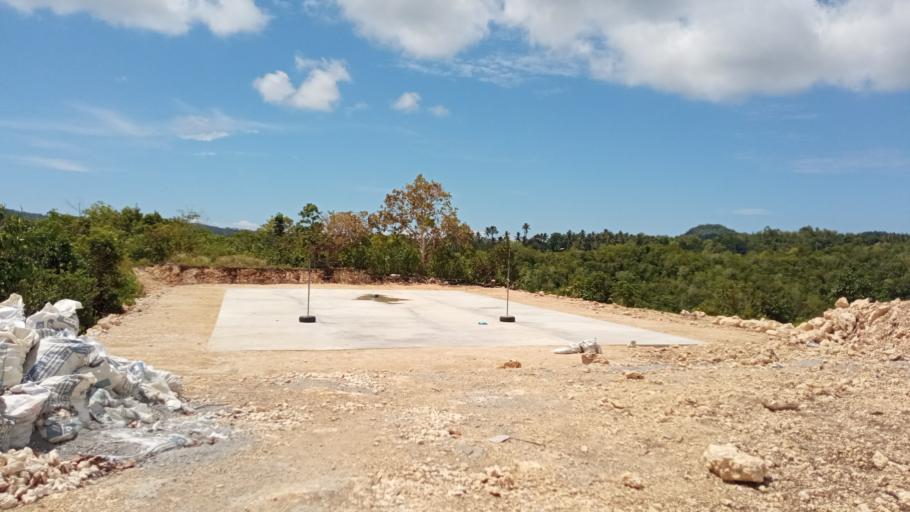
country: PH
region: Central Visayas
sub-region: Province of Siquijor
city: Lazi
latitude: 9.1490
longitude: 123.5836
